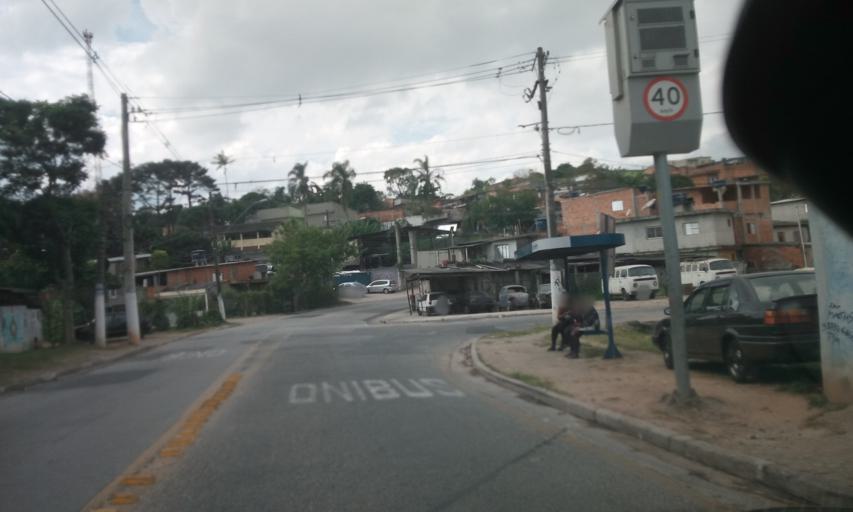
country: BR
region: Sao Paulo
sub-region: Sao Bernardo Do Campo
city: Sao Bernardo do Campo
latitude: -23.7718
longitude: -46.6027
